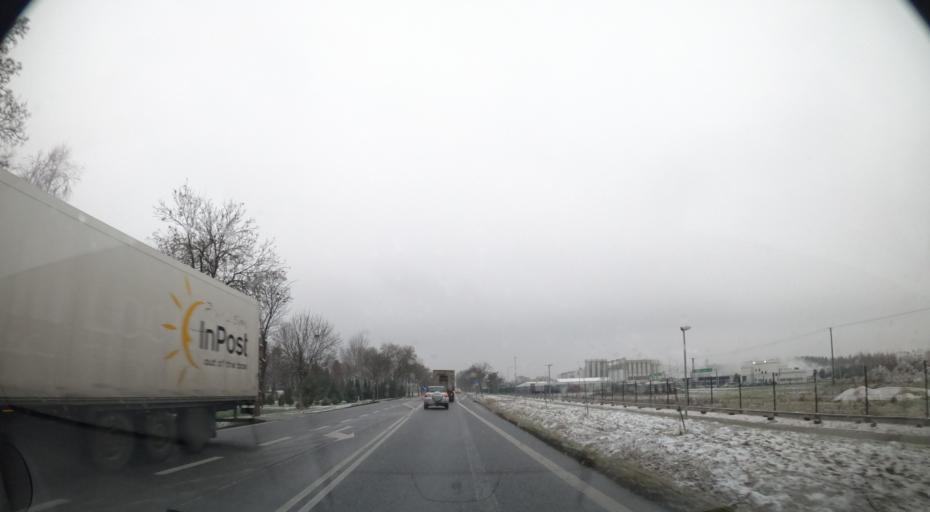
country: PL
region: Masovian Voivodeship
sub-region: Powiat sochaczewski
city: Teresin
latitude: 52.2207
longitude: 20.3341
